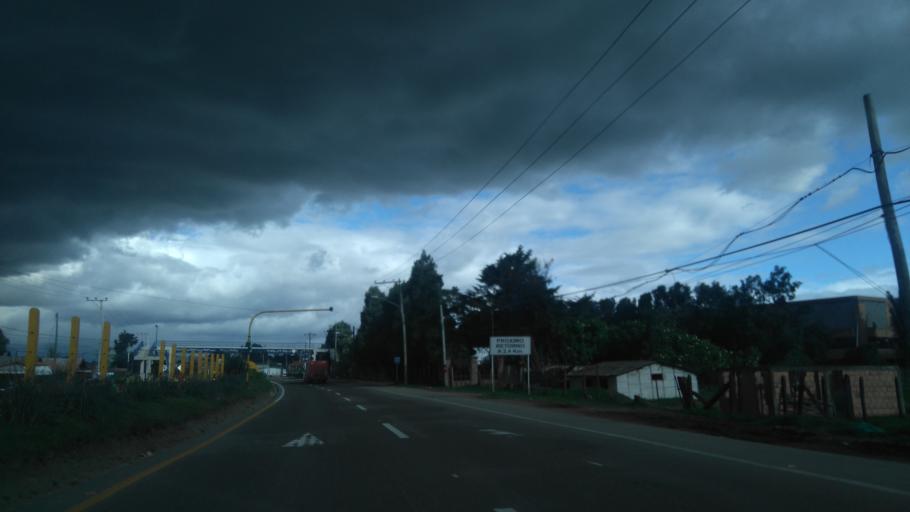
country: CO
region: Cundinamarca
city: El Rosal
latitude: 4.7997
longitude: -74.2093
